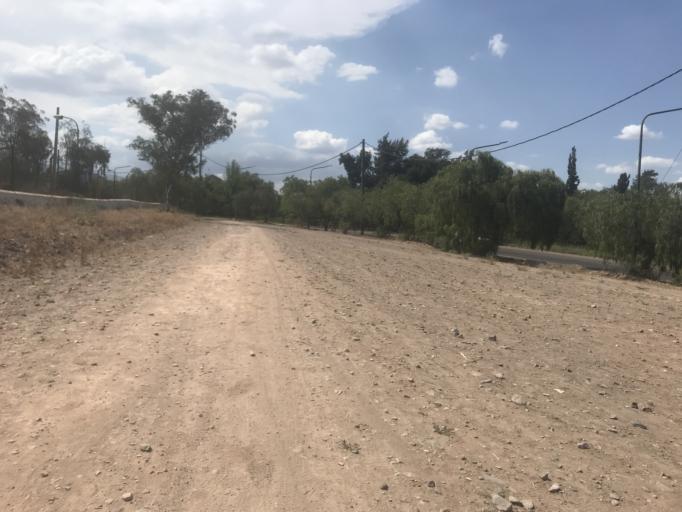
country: AR
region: Mendoza
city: Mendoza
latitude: -32.8850
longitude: -68.8851
